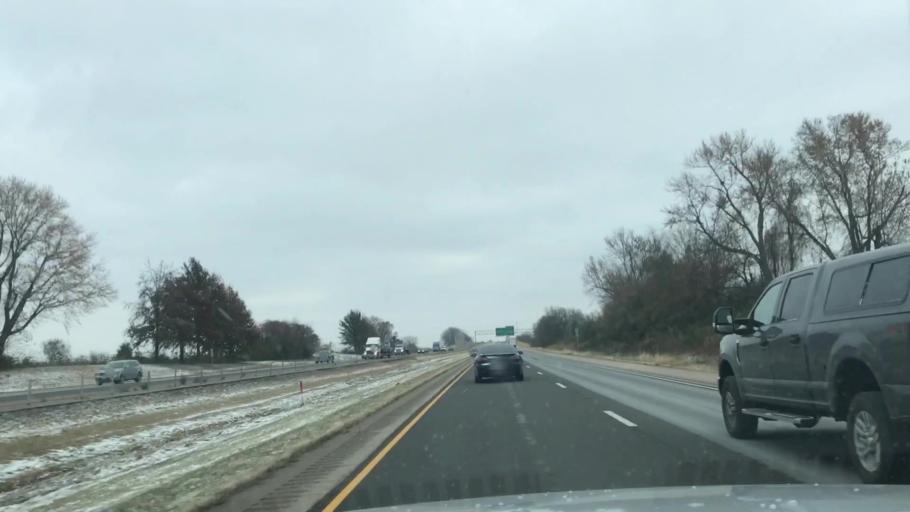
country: US
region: Illinois
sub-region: Madison County
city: Maryville
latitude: 38.7529
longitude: -89.9388
